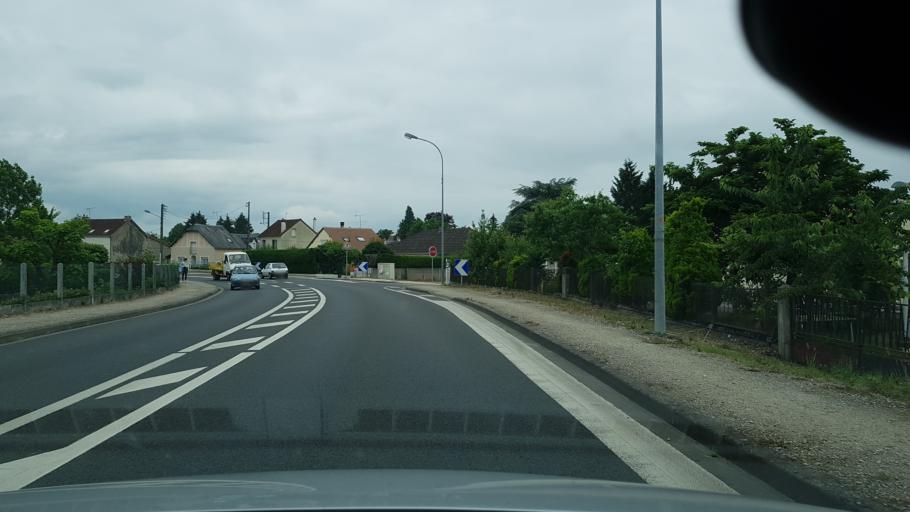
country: FR
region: Centre
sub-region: Departement du Loir-et-Cher
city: Selles-sur-Cher
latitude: 47.2816
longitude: 1.5431
